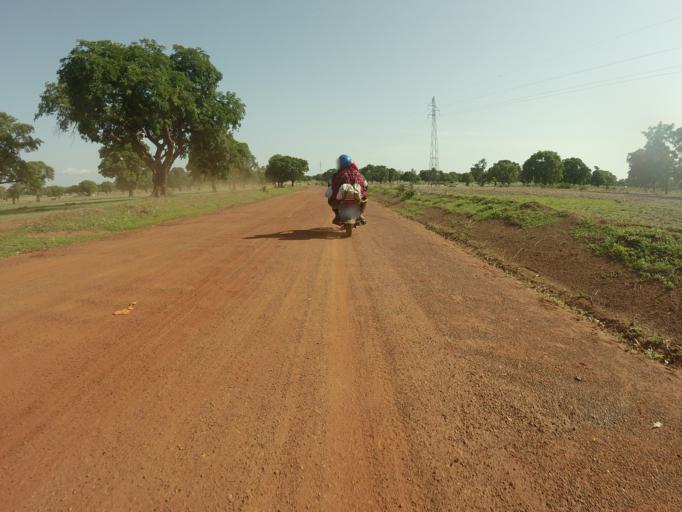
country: GH
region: Upper East
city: Bawku
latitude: 10.7785
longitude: -0.1920
